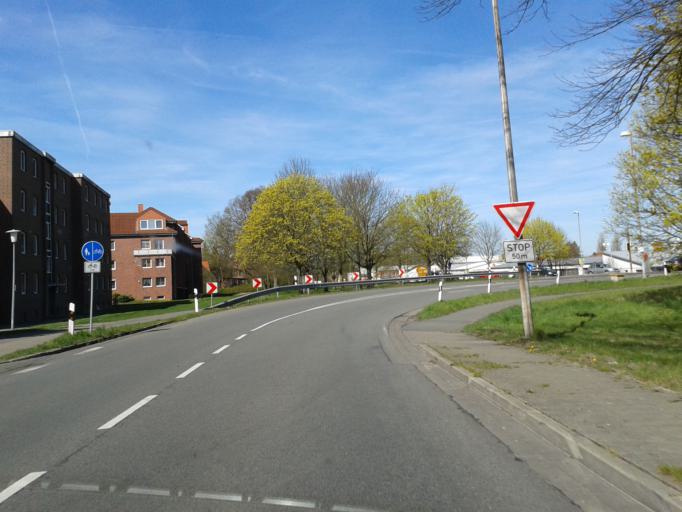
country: DE
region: Lower Saxony
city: Uelzen
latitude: 52.9628
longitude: 10.5801
